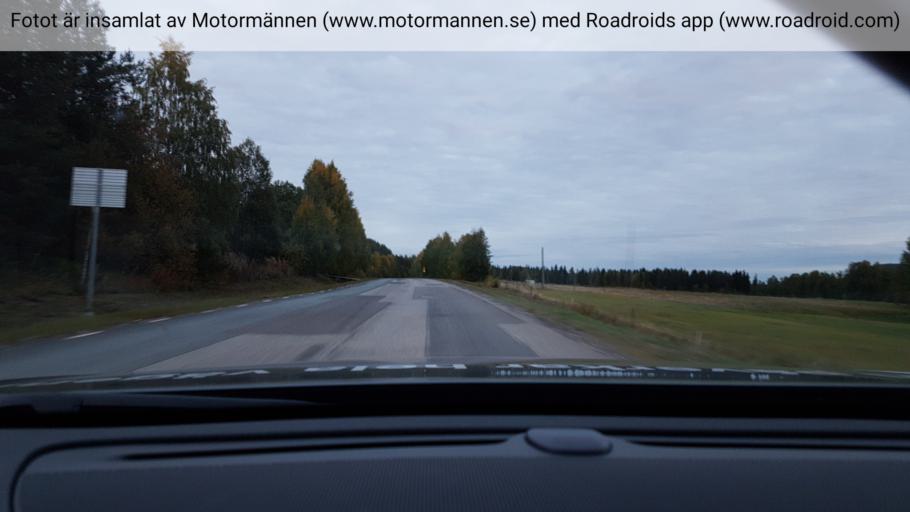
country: SE
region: Norrbotten
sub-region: Alvsbyns Kommun
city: AElvsbyn
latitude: 65.8538
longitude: 20.4372
